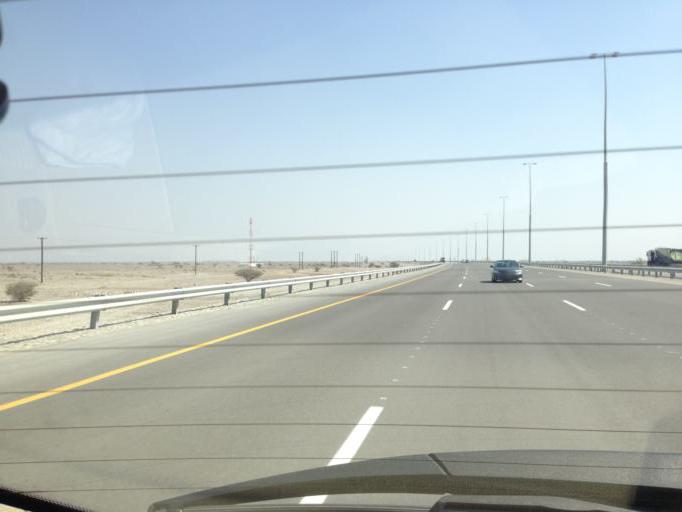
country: OM
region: Al Batinah
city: Barka'
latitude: 23.5826
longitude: 57.7948
